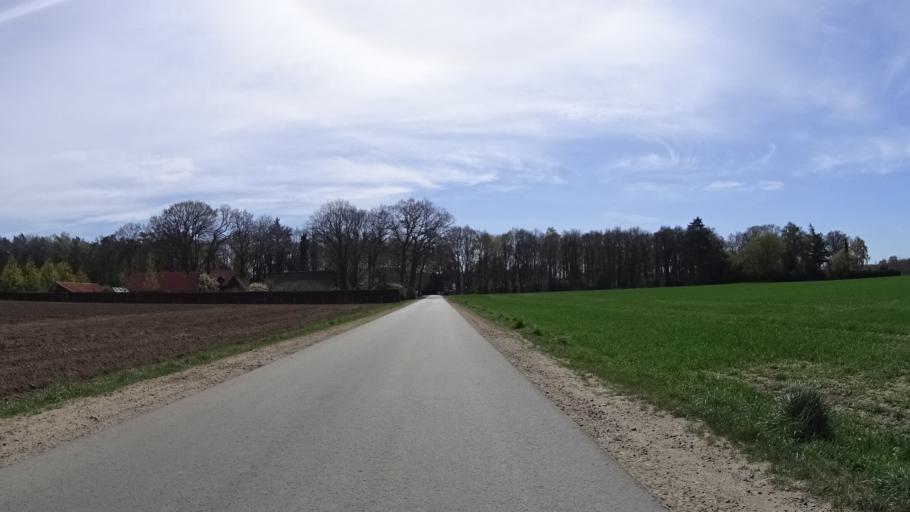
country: DE
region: Lower Saxony
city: Emsburen
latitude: 52.4426
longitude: 7.3435
